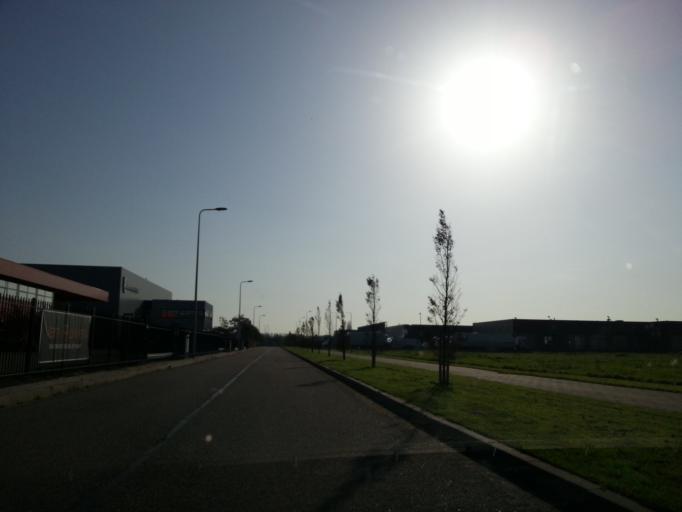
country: NL
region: South Holland
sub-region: Gemeente Lansingerland
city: Berkel en Rodenrijs
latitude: 51.9809
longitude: 4.4530
